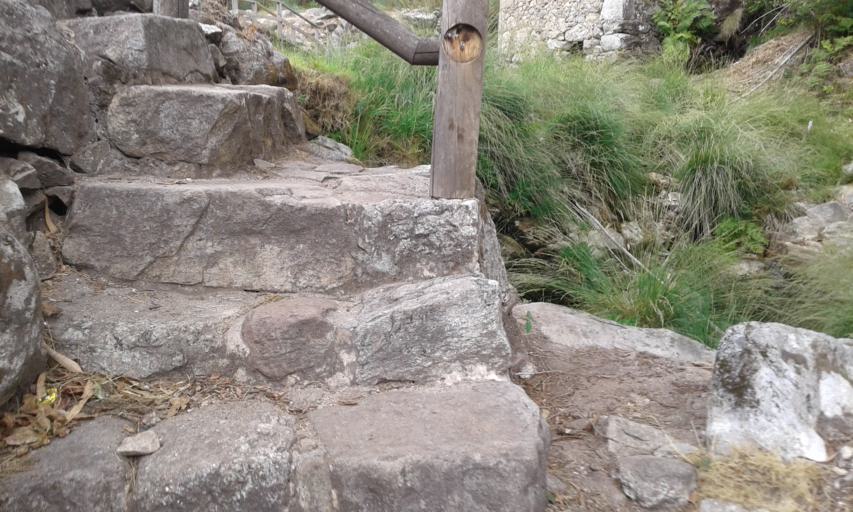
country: ES
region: Galicia
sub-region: Provincia de Pontevedra
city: O Rosal
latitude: 41.9575
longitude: -8.8410
